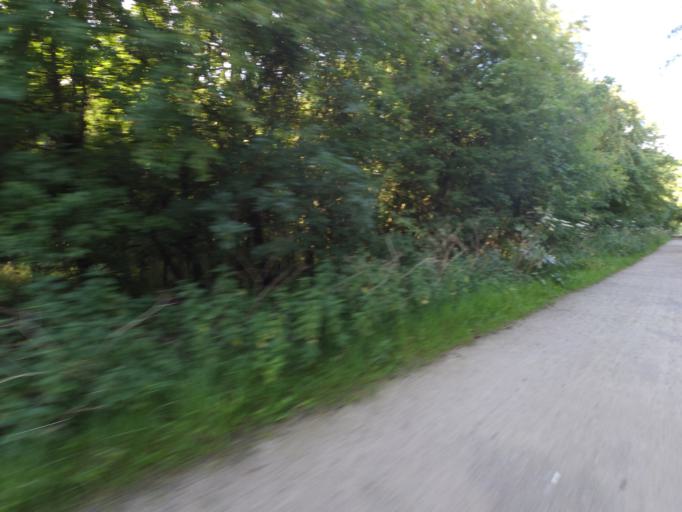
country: GB
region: England
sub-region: Staffordshire
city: Stafford
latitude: 52.8048
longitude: -2.1590
